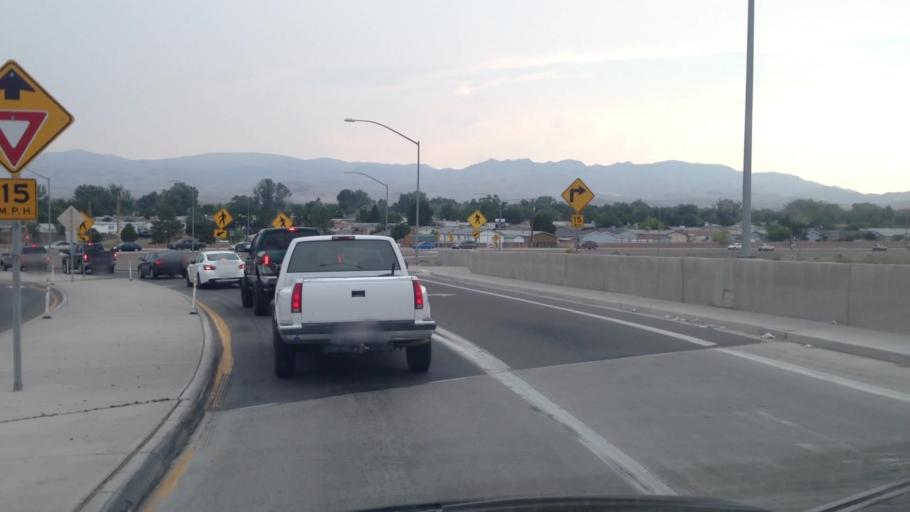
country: US
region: Nevada
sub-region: Lyon County
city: Fernley
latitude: 39.6047
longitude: -119.2266
